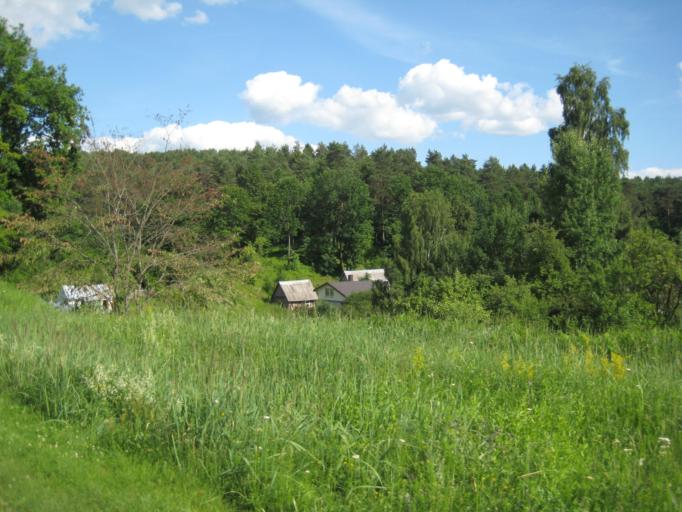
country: LT
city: Baltoji Voke
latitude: 54.6324
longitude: 25.1996
